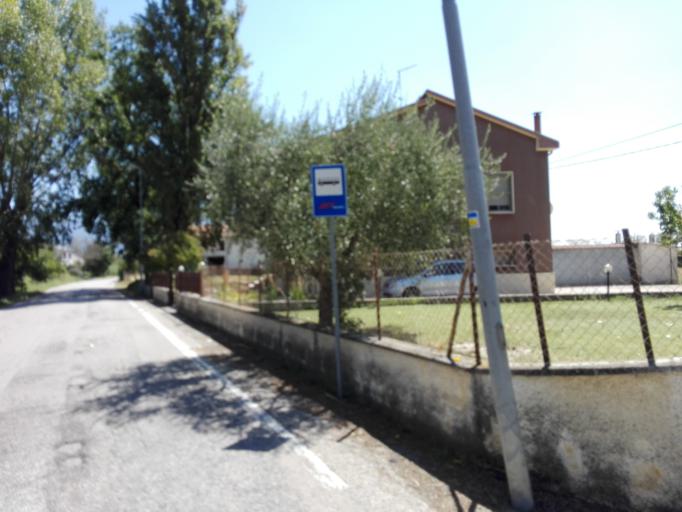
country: IT
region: Umbria
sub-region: Provincia di Perugia
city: Foligno
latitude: 42.9493
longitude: 12.6782
